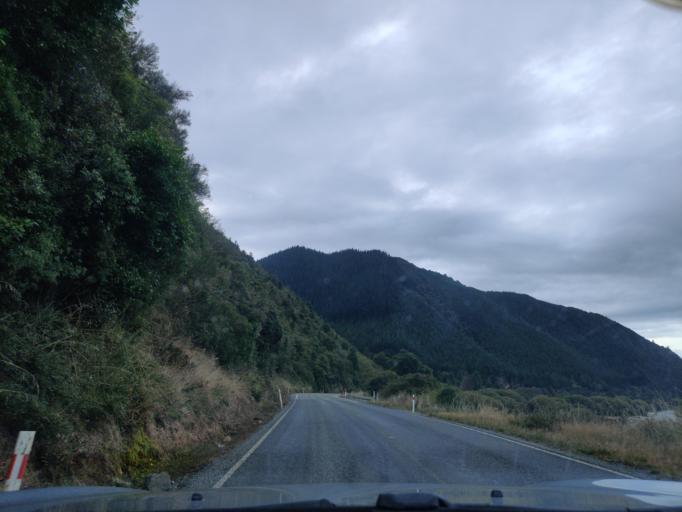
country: NZ
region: Tasman
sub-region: Tasman District
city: Wakefield
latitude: -41.6976
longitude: 172.6324
